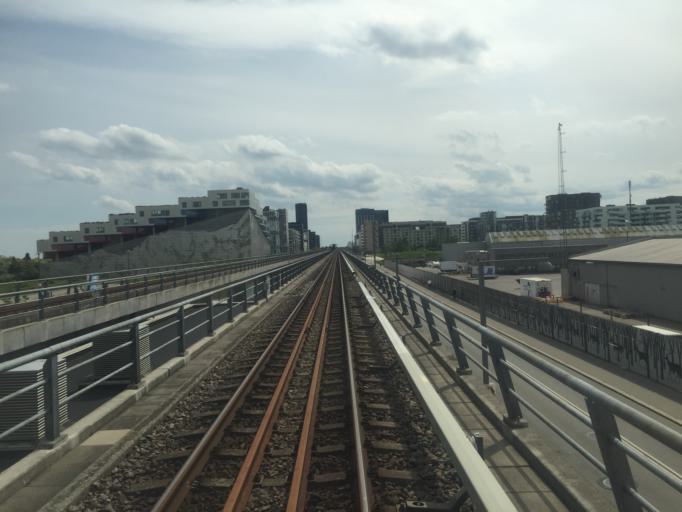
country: DK
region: Capital Region
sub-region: Tarnby Kommune
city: Tarnby
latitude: 55.6378
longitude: 12.5825
